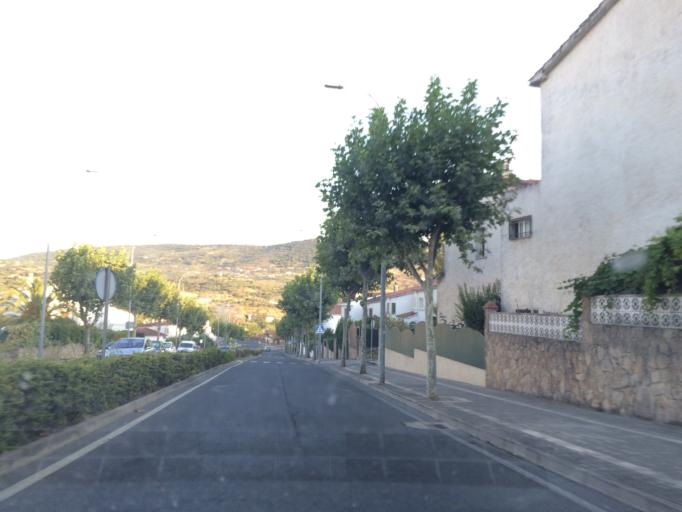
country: ES
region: Extremadura
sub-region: Provincia de Caceres
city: Plasencia
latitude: 40.0366
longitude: -6.0786
